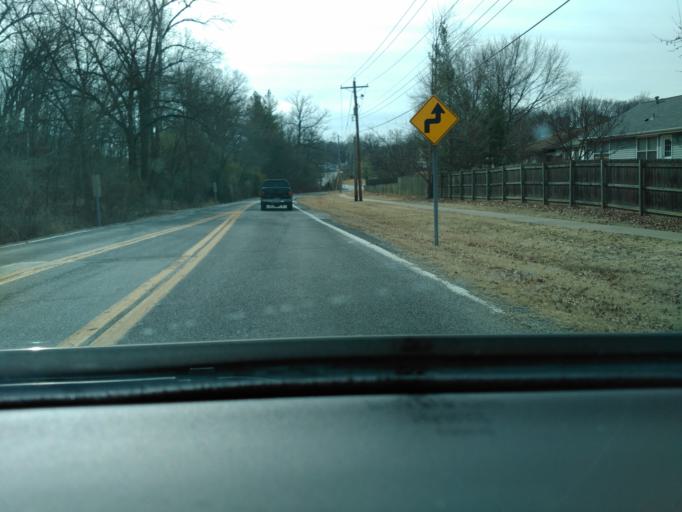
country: US
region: Missouri
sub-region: Saint Louis County
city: Valley Park
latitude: 38.5561
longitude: -90.5112
